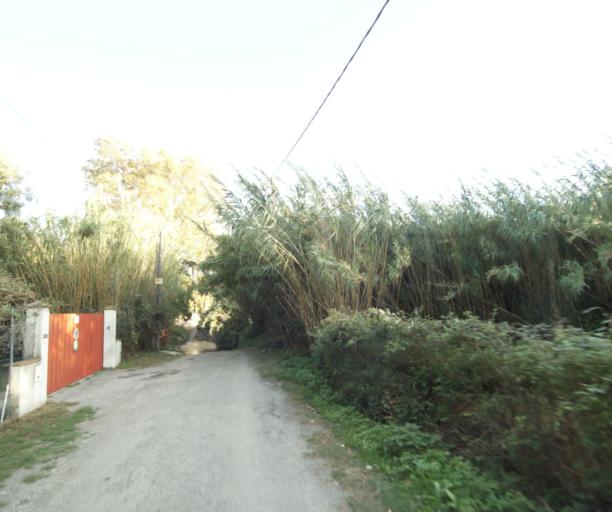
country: FR
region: Languedoc-Roussillon
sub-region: Departement des Pyrenees-Orientales
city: Sant Andreu de Sureda
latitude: 42.5702
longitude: 2.9884
